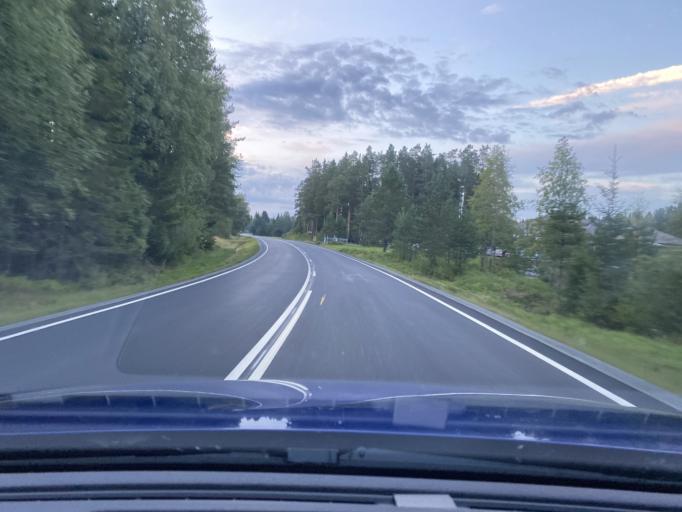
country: FI
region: Satakunta
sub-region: Pohjois-Satakunta
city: Honkajoki
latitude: 62.0700
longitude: 22.2498
